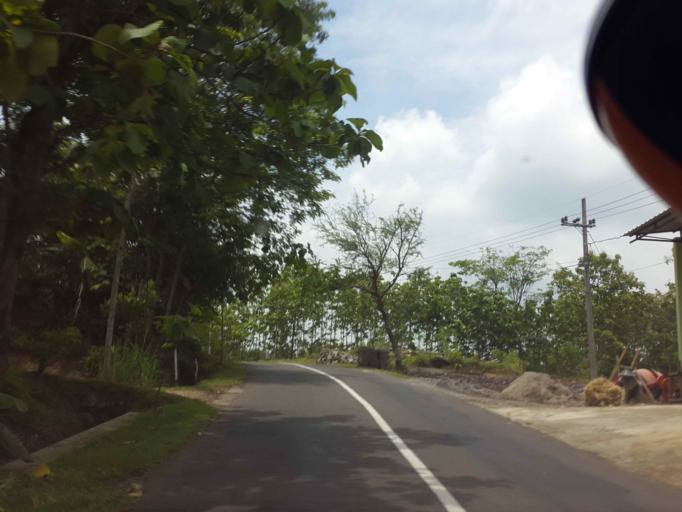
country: ID
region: East Java
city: Madiun
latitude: -7.6998
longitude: 111.3445
